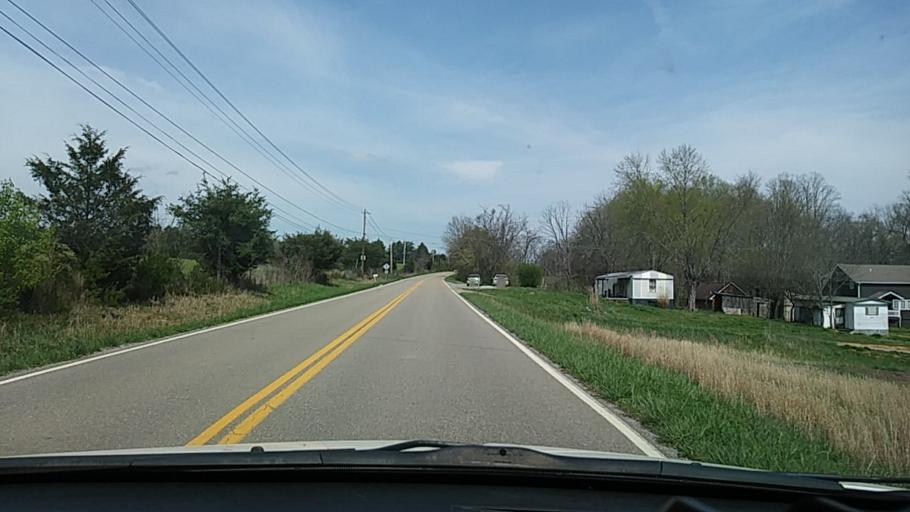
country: US
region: Tennessee
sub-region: Greene County
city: Greeneville
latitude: 36.0910
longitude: -82.7964
